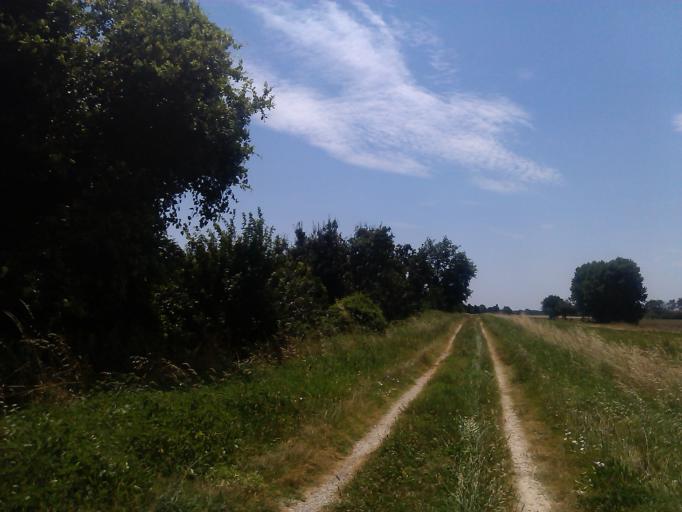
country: IT
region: Tuscany
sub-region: Province of Arezzo
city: Cesa
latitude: 43.3308
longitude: 11.8312
